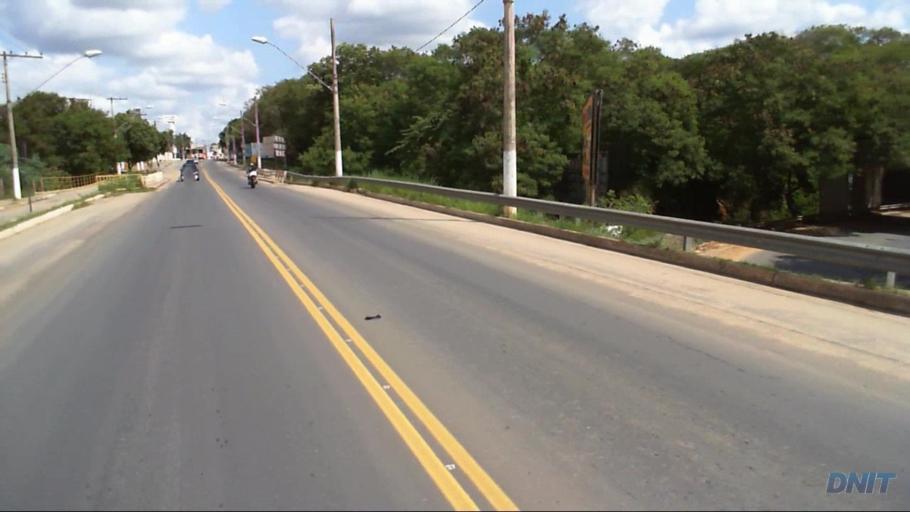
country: BR
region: Minas Gerais
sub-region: Governador Valadares
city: Governador Valadares
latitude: -18.8873
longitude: -41.9711
